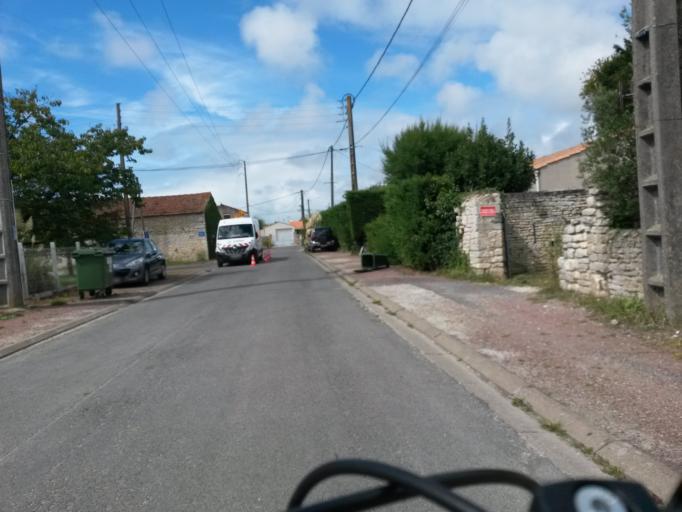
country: FR
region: Poitou-Charentes
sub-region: Departement de la Charente-Maritime
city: Dolus-d'Oleron
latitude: 45.9483
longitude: -1.3012
